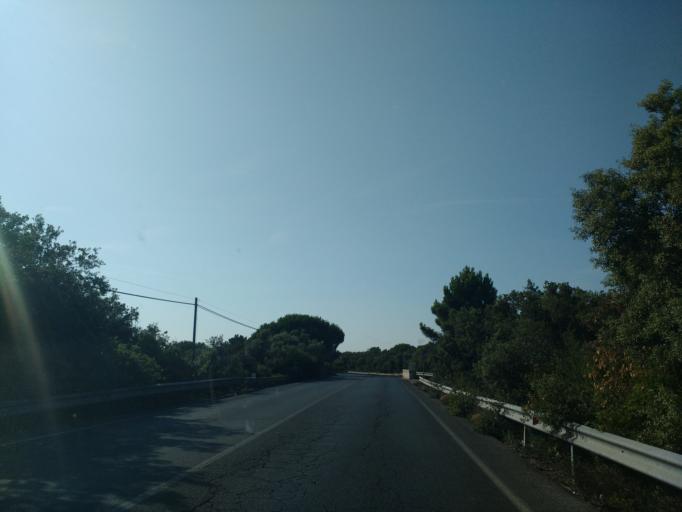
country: IT
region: Latium
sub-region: Citta metropolitana di Roma Capitale
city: Acilia-Castel Fusano-Ostia Antica
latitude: 41.6936
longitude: 12.3654
